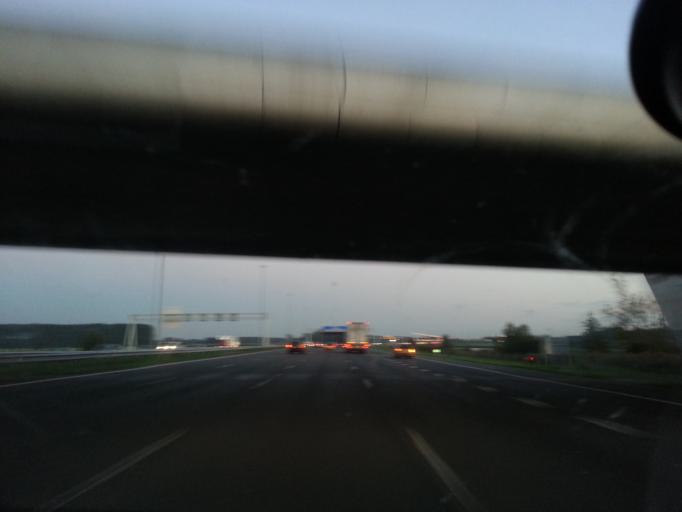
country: NL
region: Gelderland
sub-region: Gemeente Culemborg
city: Culemborg
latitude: 51.9376
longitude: 5.1540
